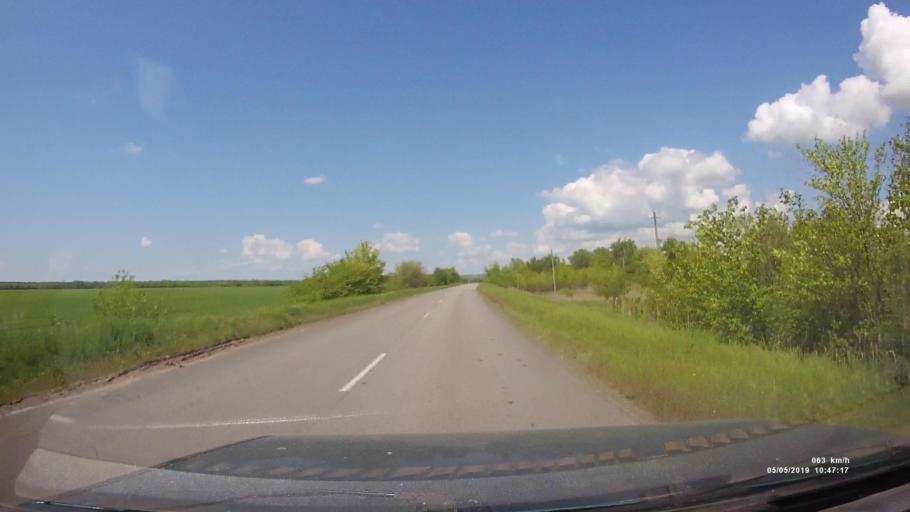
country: RU
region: Rostov
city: Ust'-Donetskiy
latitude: 47.6379
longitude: 40.8349
